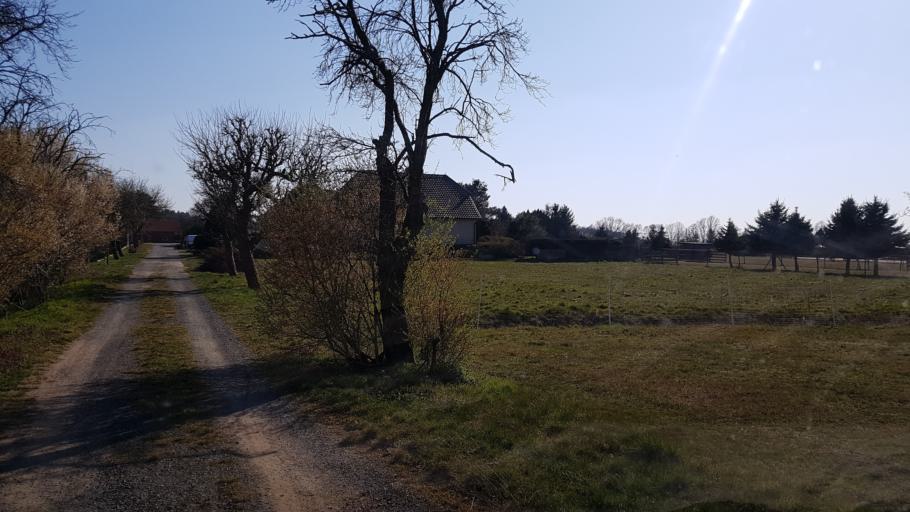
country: DE
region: Brandenburg
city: Sonnewalde
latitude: 51.6786
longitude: 13.6805
